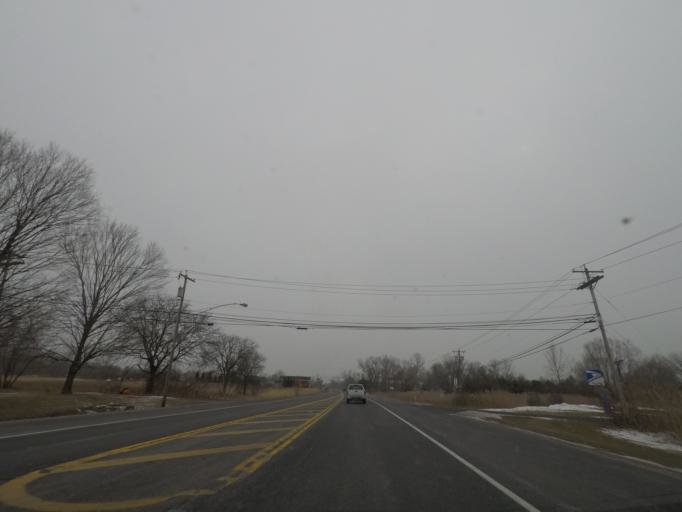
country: US
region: New York
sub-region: Rensselaer County
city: Castleton-on-Hudson
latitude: 42.5545
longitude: -73.8086
